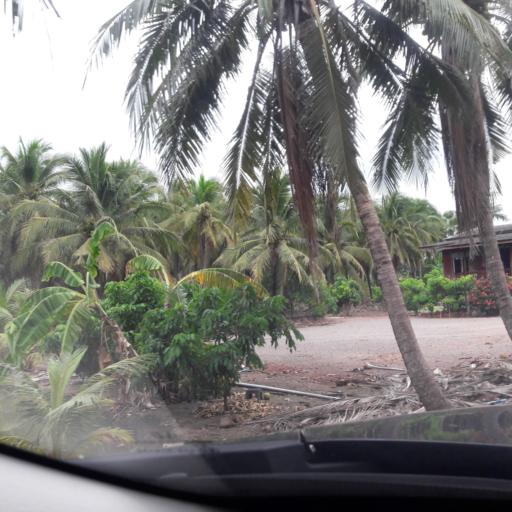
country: TH
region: Ratchaburi
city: Damnoen Saduak
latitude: 13.5730
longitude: 99.9466
